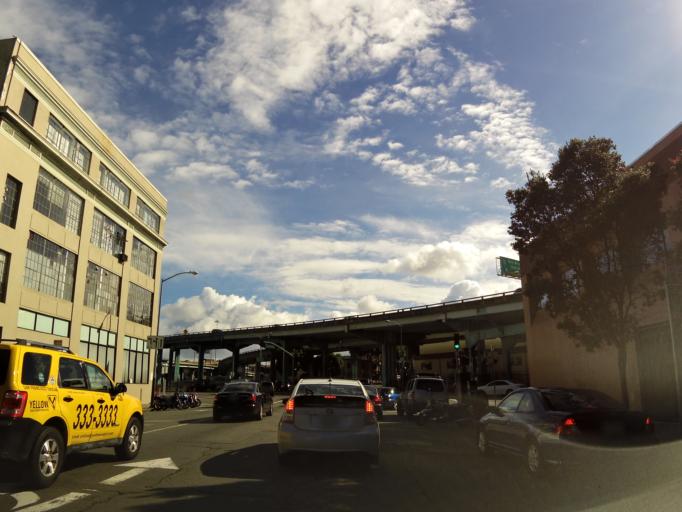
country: US
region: California
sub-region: San Francisco County
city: San Francisco
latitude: 37.7696
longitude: -122.4089
